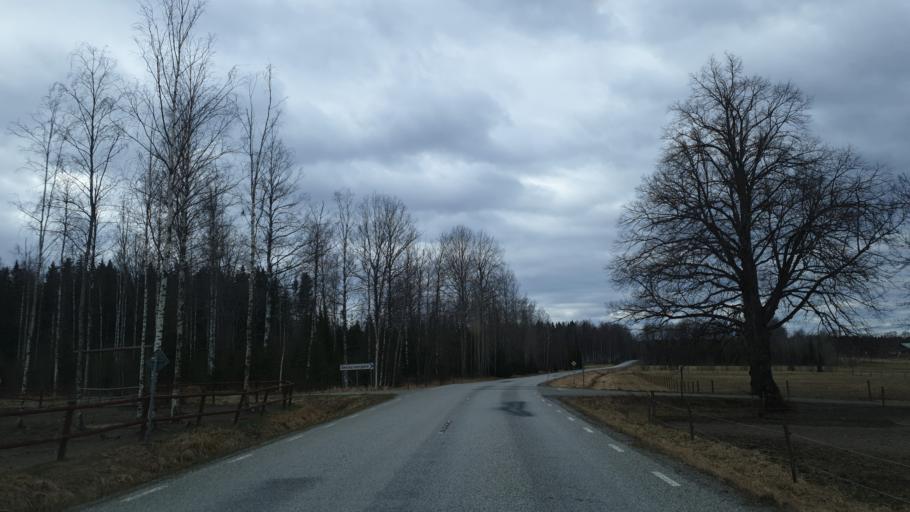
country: SE
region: OErebro
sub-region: Nora Kommun
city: As
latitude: 59.5819
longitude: 14.9692
